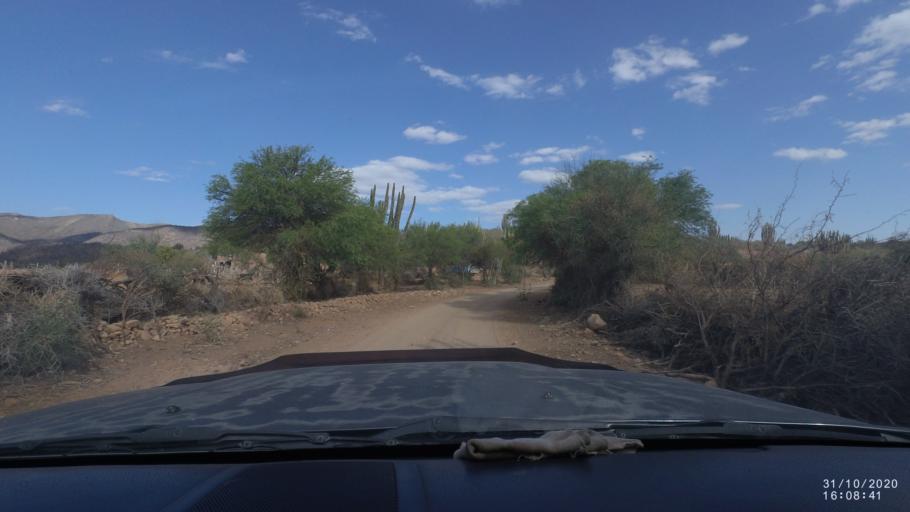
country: BO
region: Chuquisaca
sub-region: Provincia Zudanez
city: Mojocoya
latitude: -18.3849
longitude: -64.6394
